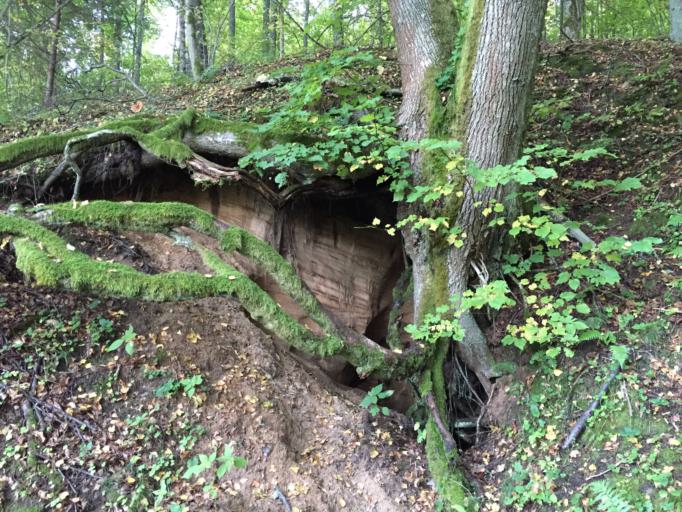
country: LV
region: Seja
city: Loja
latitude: 57.1324
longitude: 24.6164
